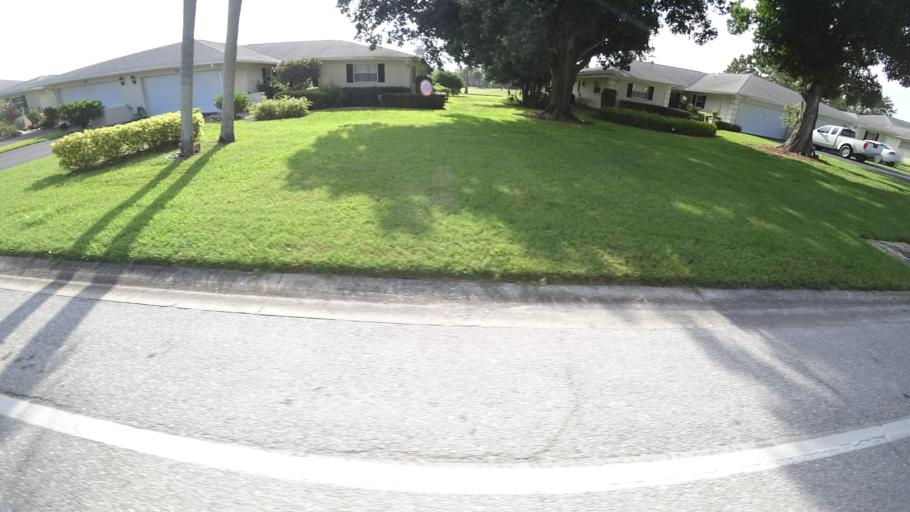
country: US
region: Florida
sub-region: Sarasota County
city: Desoto Lakes
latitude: 27.4151
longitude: -82.4966
